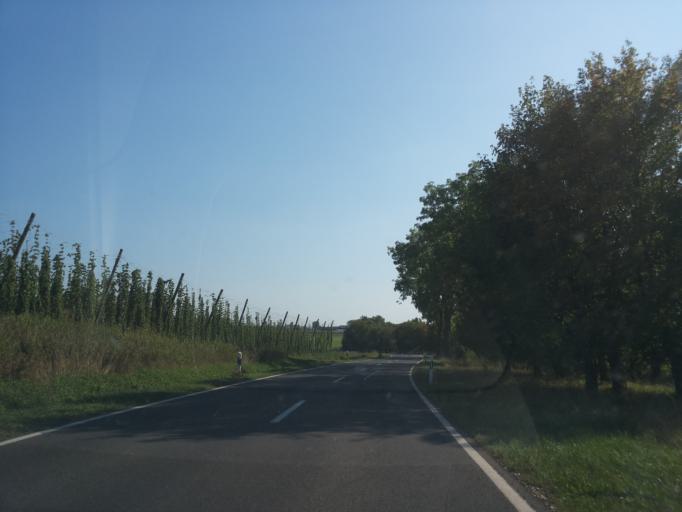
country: DE
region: Bavaria
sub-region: Lower Bavaria
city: Neustadt an der Donau
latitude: 48.8414
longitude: 11.7719
